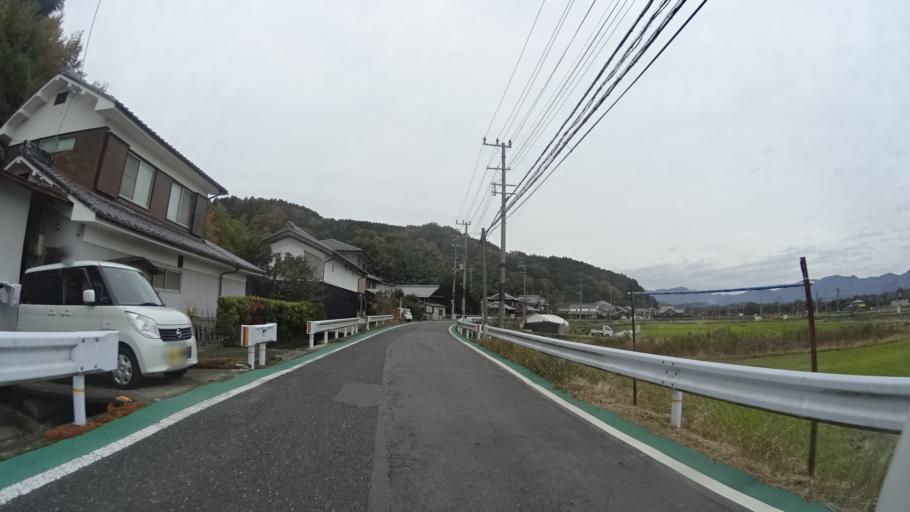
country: JP
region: Kyoto
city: Kameoka
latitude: 35.0556
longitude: 135.5456
